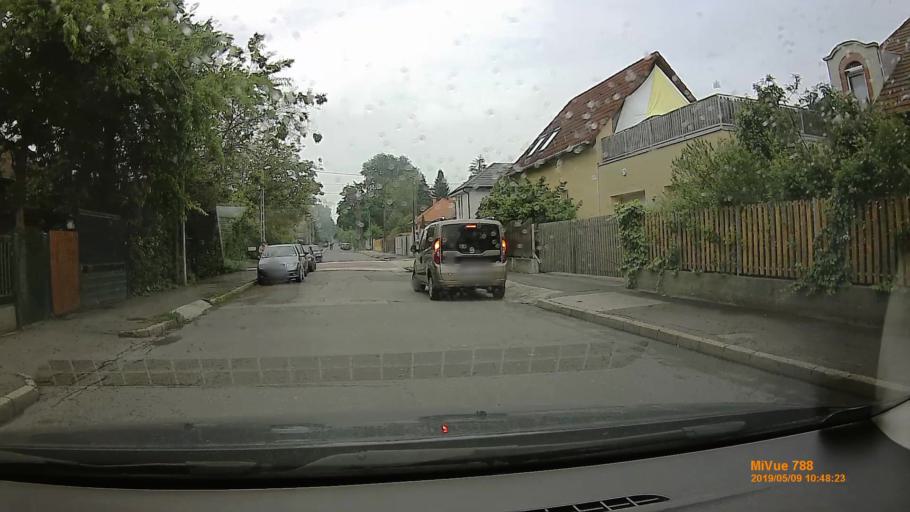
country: HU
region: Budapest
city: Budapest XVI. keruelet
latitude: 47.5190
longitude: 19.1547
